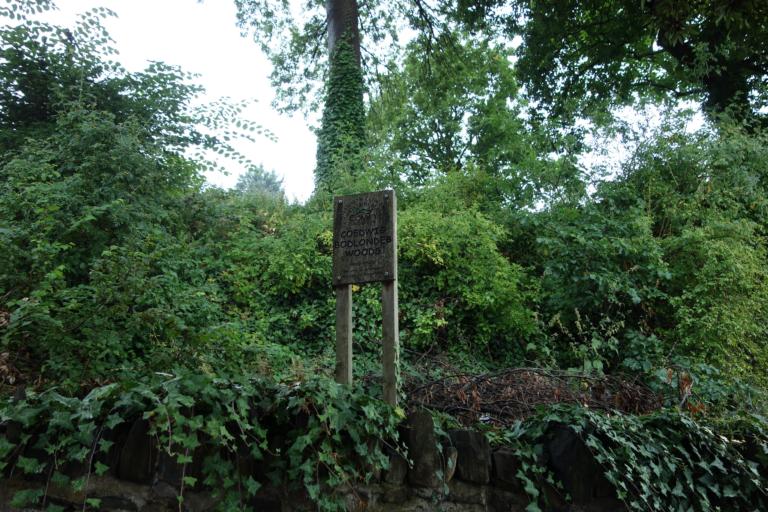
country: GB
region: Wales
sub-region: Conwy
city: Conwy
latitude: 53.2843
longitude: -3.8304
